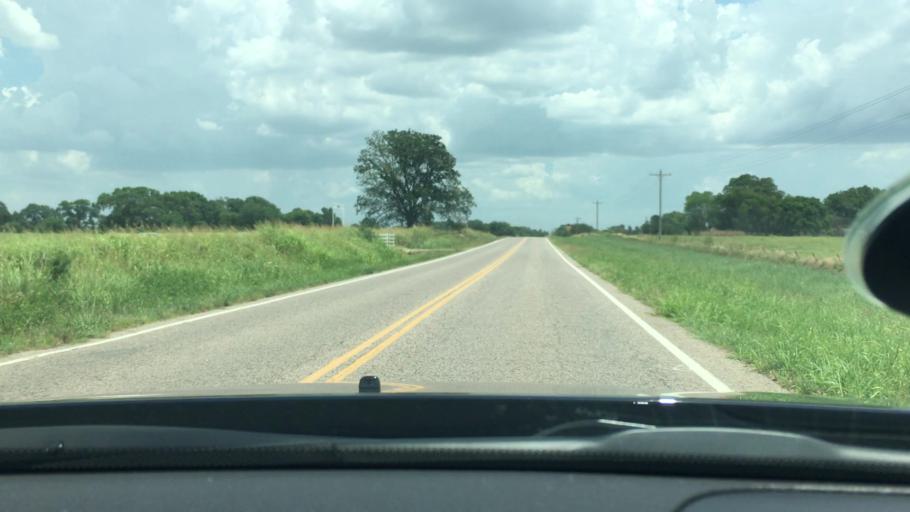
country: US
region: Texas
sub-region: Grayson County
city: Sherwood Shores
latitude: 33.9840
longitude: -96.9259
